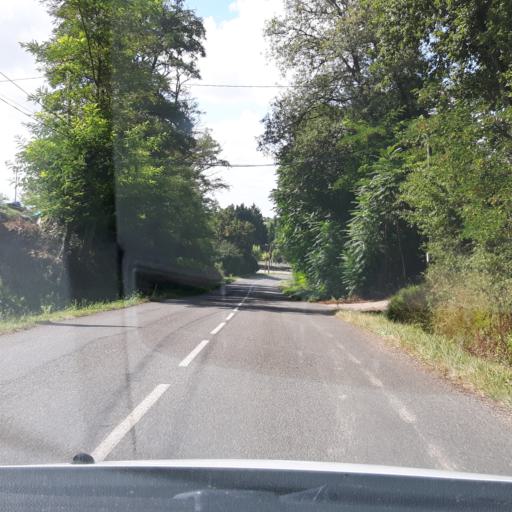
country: FR
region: Midi-Pyrenees
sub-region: Departement de la Haute-Garonne
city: Bouloc
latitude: 43.7915
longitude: 1.4133
